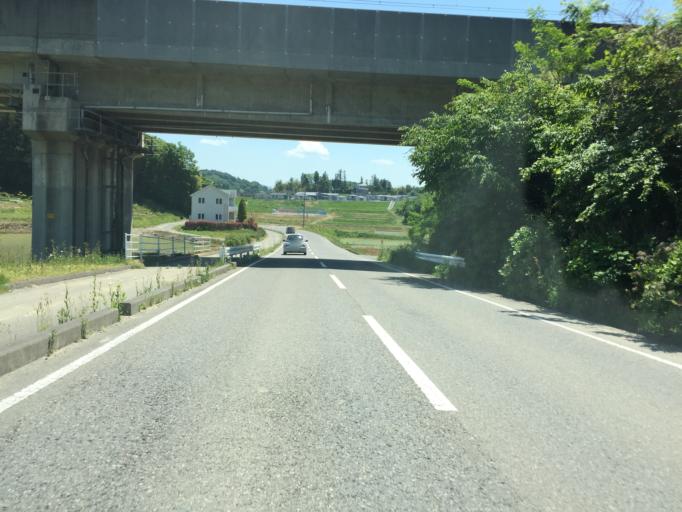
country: JP
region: Fukushima
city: Motomiya
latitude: 37.5268
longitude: 140.4372
